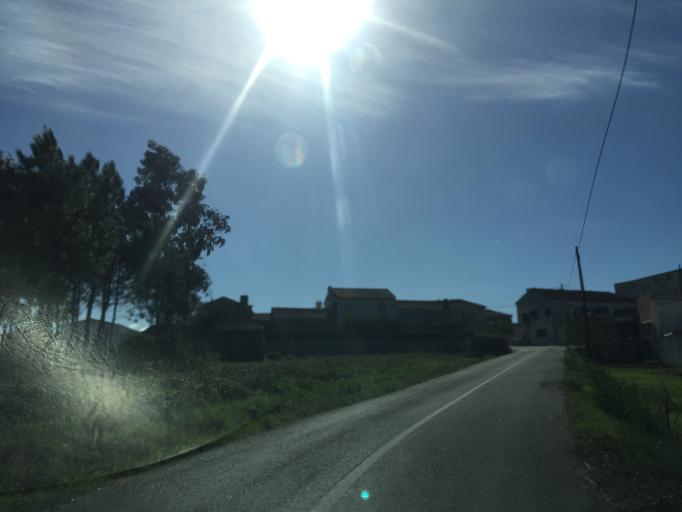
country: PT
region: Coimbra
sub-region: Figueira da Foz
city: Tavarede
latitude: 40.1917
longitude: -8.8637
